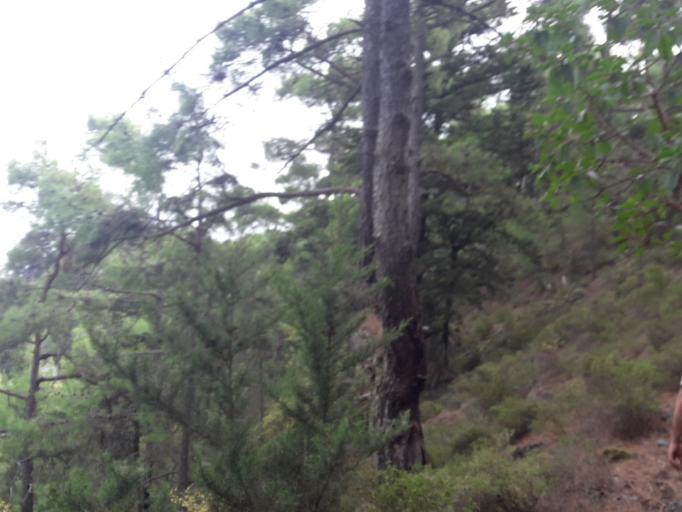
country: CY
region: Ammochostos
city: Lefkonoiko
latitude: 35.2941
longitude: 33.5472
